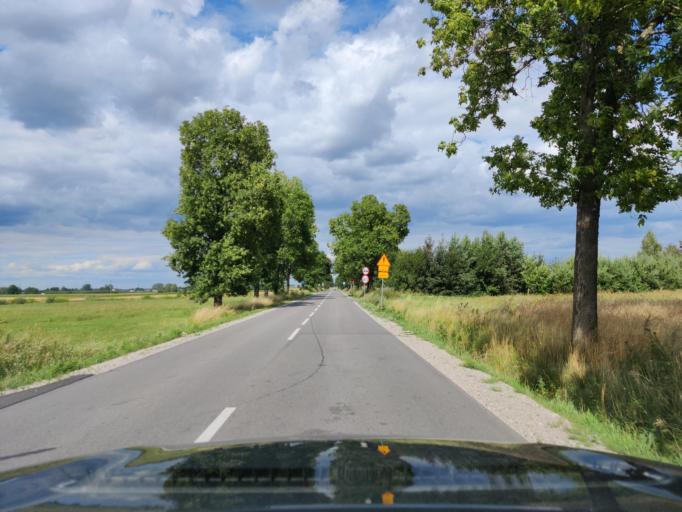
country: PL
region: Masovian Voivodeship
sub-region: Powiat sokolowski
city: Kosow Lacki
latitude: 52.5613
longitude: 22.1157
